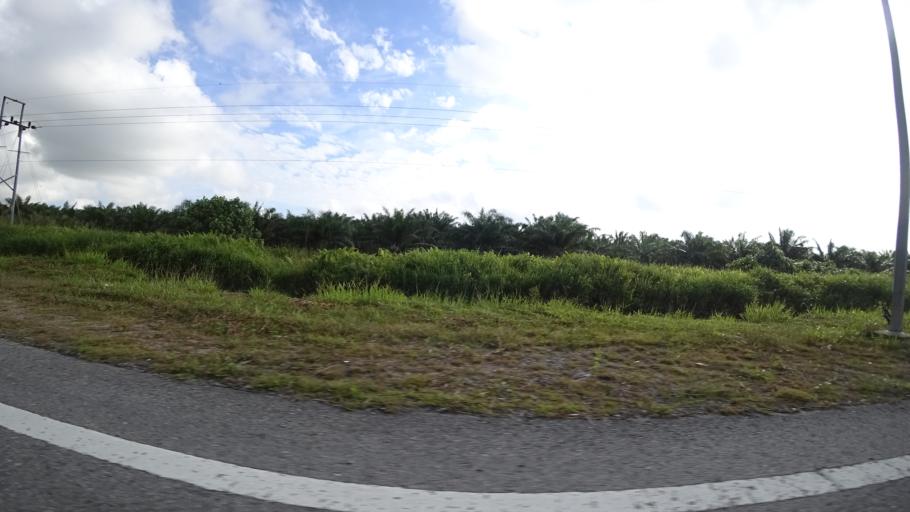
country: MY
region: Sarawak
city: Miri
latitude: 4.5356
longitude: 113.9846
